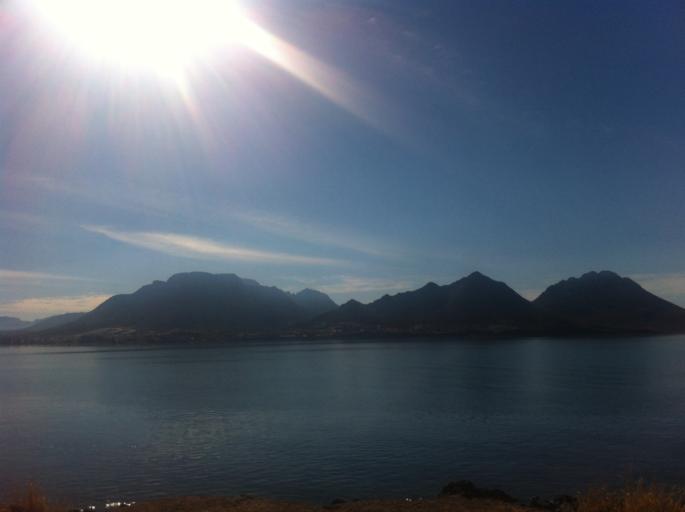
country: MX
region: Sonora
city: Heroica Guaymas
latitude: 27.9261
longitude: -110.9577
